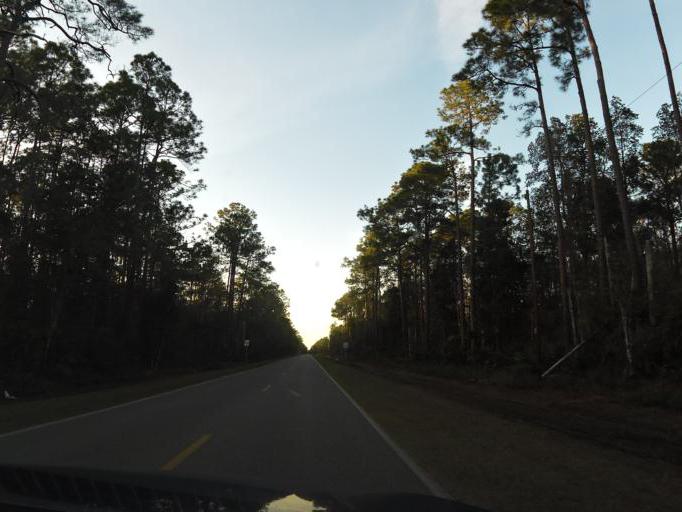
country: US
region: Florida
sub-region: Clay County
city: Green Cove Springs
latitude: 29.8747
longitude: -81.5507
